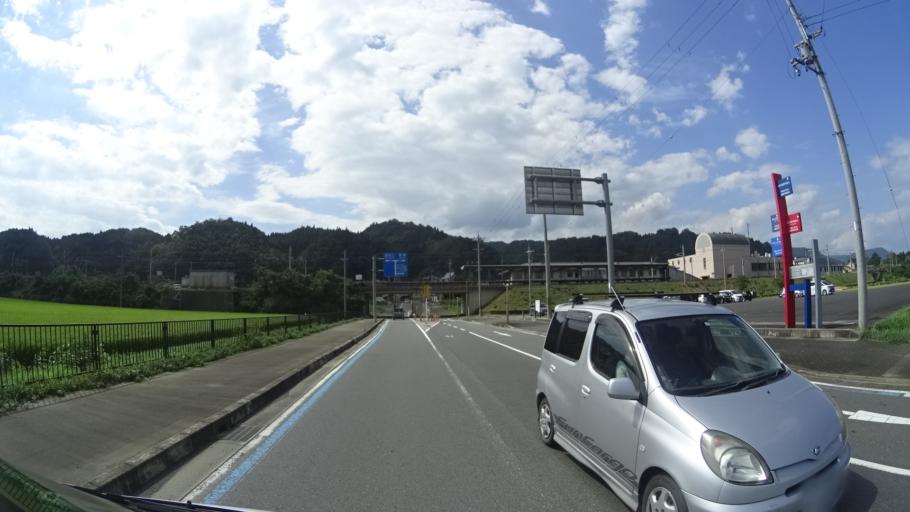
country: JP
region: Kyoto
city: Fukuchiyama
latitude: 35.3880
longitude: 135.1482
